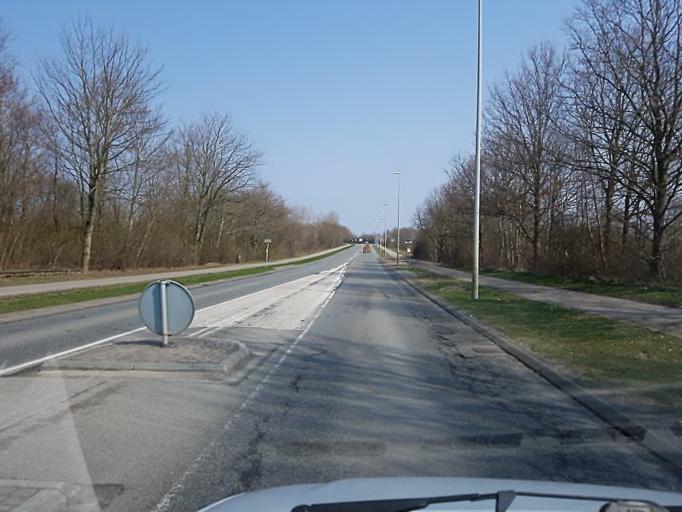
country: DK
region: South Denmark
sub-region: Esbjerg Kommune
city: Esbjerg
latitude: 55.4940
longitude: 8.4658
